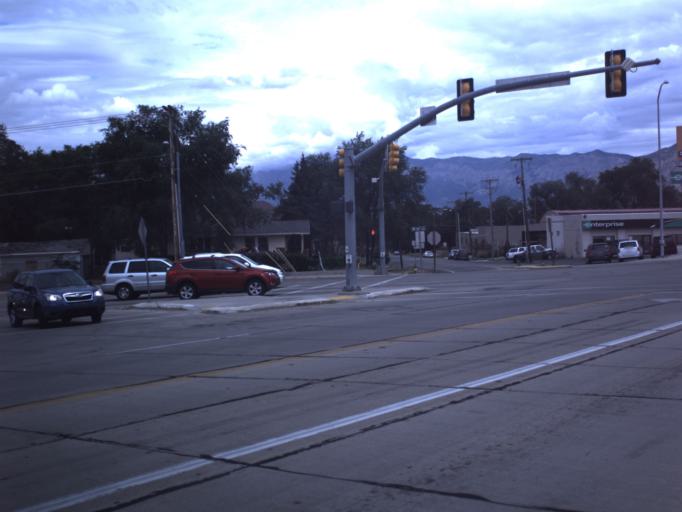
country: US
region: Utah
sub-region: Weber County
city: South Ogden
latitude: 41.1974
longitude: -111.9740
